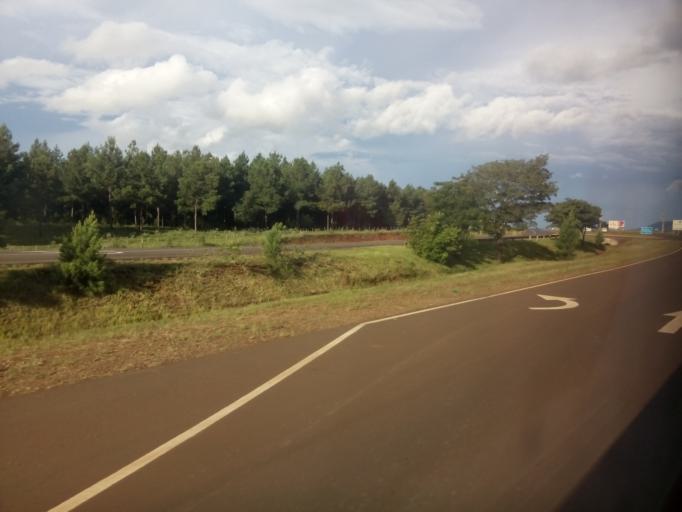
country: AR
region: Misiones
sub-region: Departamento de Candelaria
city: Candelaria
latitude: -27.4626
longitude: -55.6815
